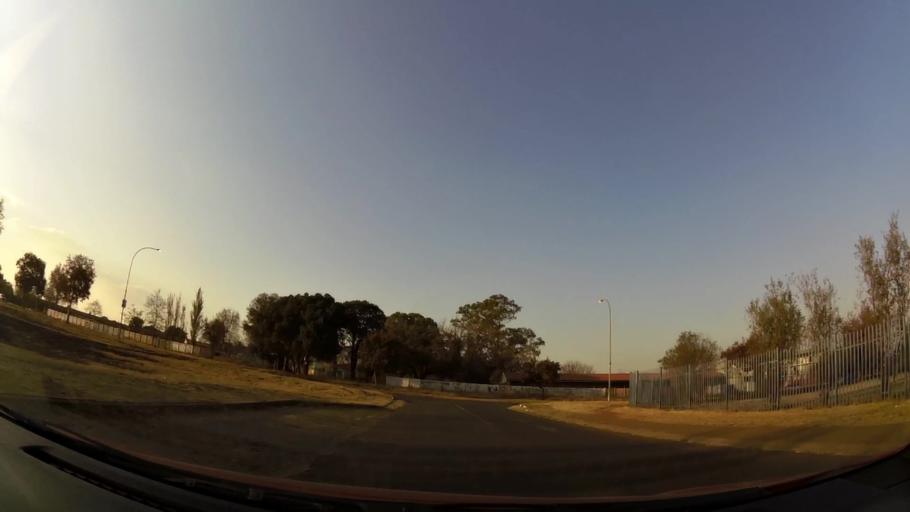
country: ZA
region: Gauteng
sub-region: City of Johannesburg Metropolitan Municipality
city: Soweto
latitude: -26.2843
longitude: 27.8991
